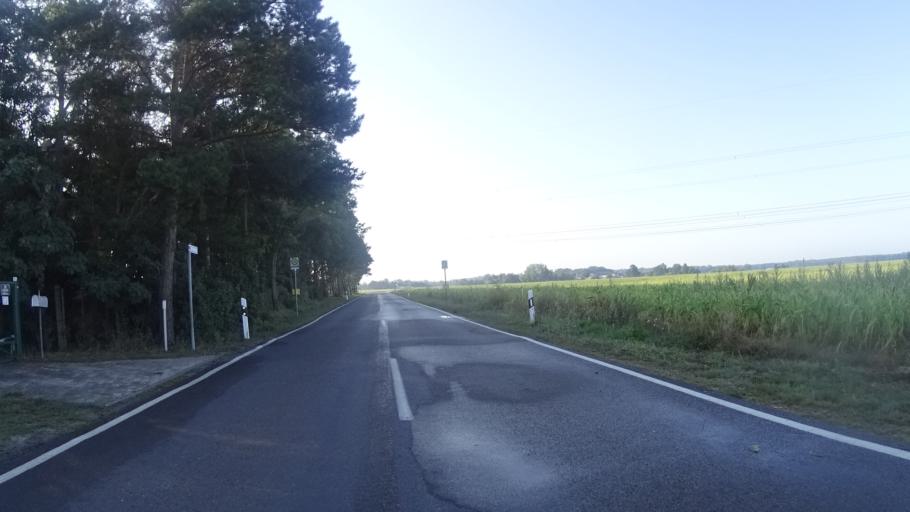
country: DE
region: Brandenburg
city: Kasel-Golzig
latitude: 51.9979
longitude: 13.6901
